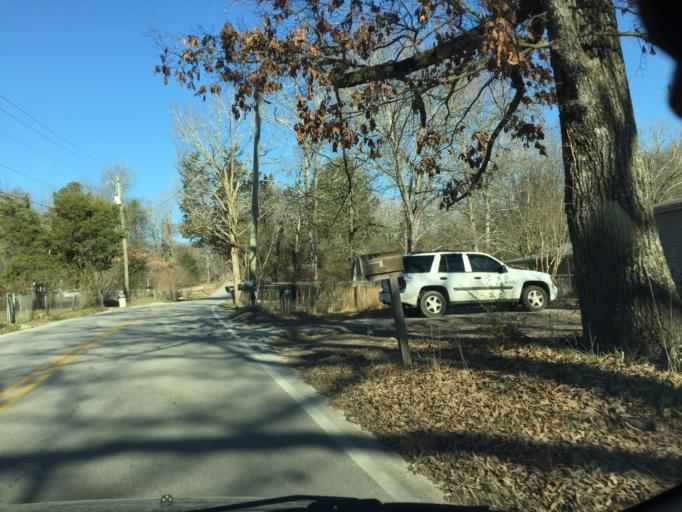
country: US
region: Tennessee
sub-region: Hamilton County
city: Collegedale
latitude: 35.0588
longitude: -85.0938
